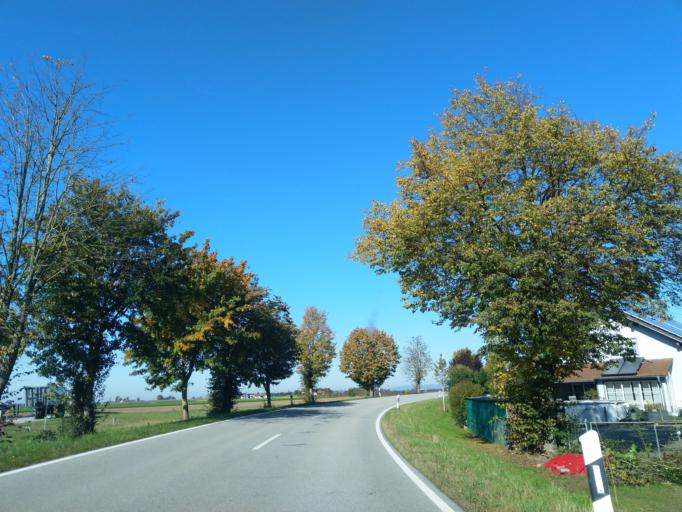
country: DE
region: Bavaria
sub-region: Lower Bavaria
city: Stephansposching
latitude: 48.8026
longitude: 12.8021
